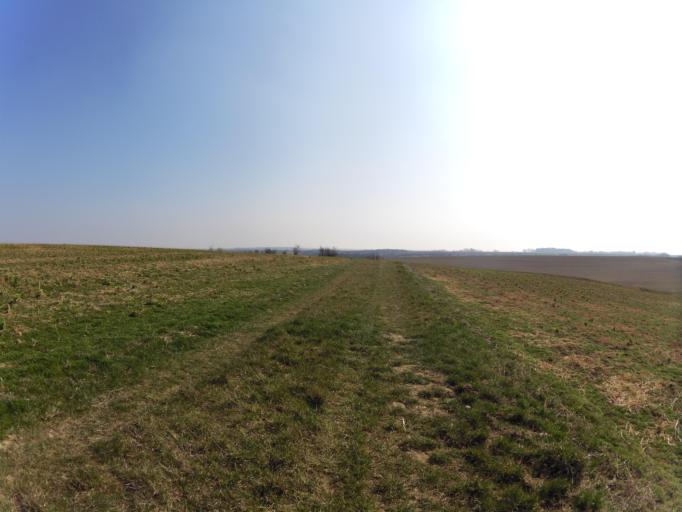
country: DE
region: Bavaria
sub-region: Regierungsbezirk Unterfranken
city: Winterhausen
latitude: 49.6823
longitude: 9.9824
